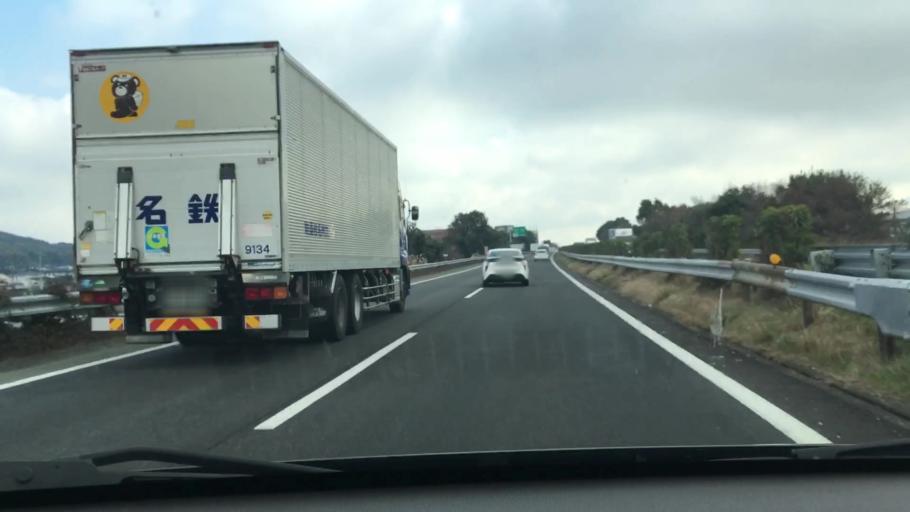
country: JP
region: Kumamoto
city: Kumamoto
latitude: 32.8424
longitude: 130.7736
